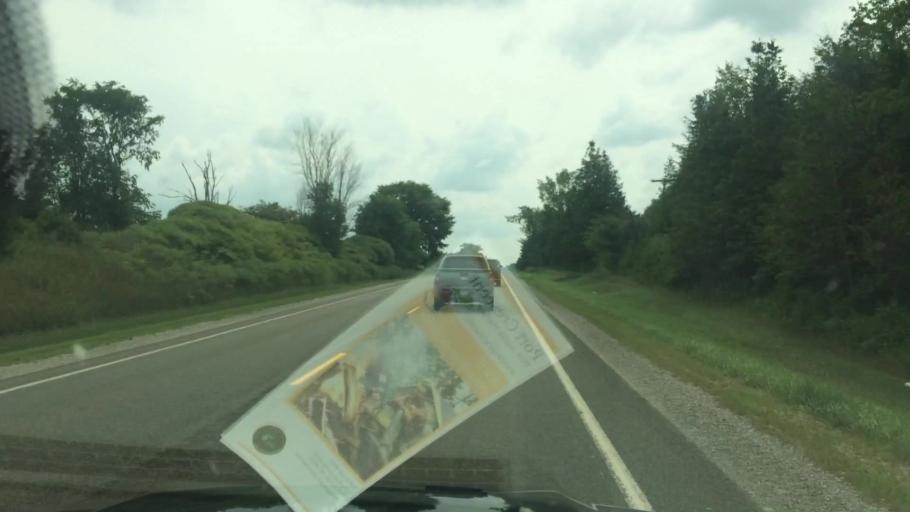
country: US
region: Michigan
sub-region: Tuscola County
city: Cass City
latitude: 43.6806
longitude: -83.0982
